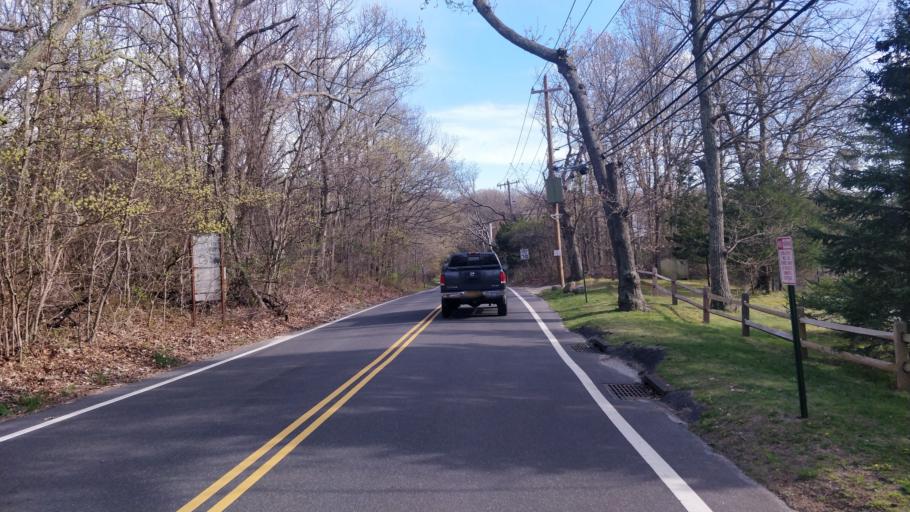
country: US
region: New York
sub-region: Suffolk County
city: Stony Brook
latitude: 40.9476
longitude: -73.1375
